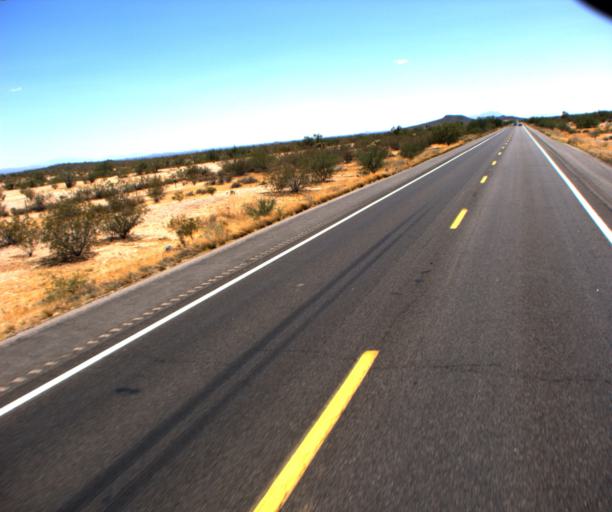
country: US
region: Arizona
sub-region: Pinal County
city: Florence
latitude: 33.1515
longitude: -111.3564
